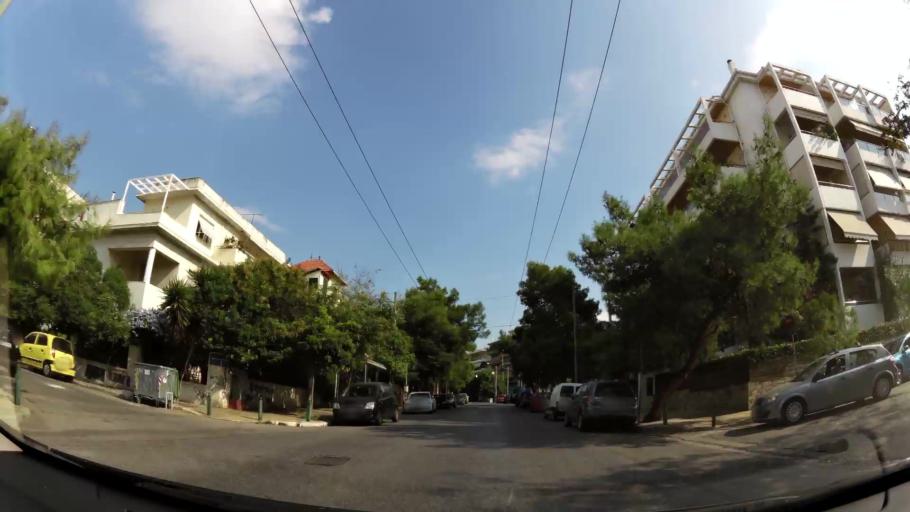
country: GR
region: Attica
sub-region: Nomarchia Athinas
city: Nea Chalkidona
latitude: 38.0195
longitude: 23.7386
